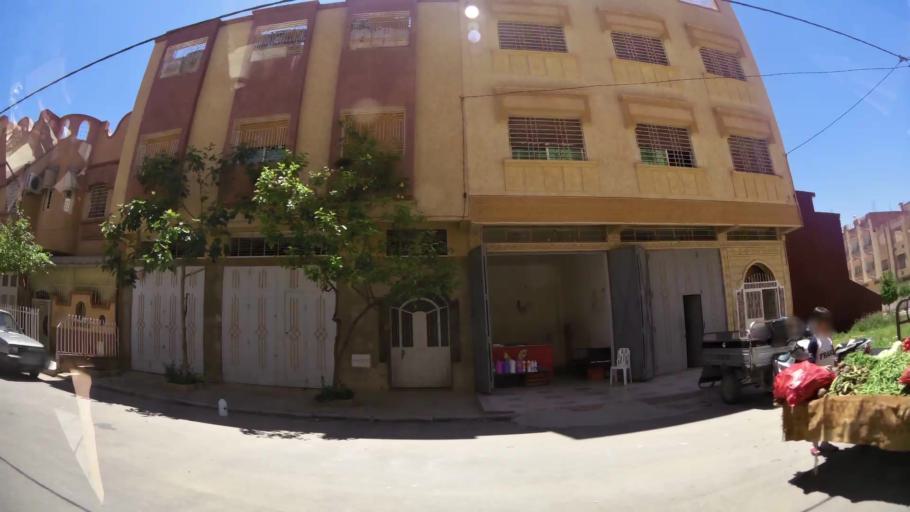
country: MA
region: Oriental
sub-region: Oujda-Angad
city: Oujda
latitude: 34.6756
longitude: -1.8777
